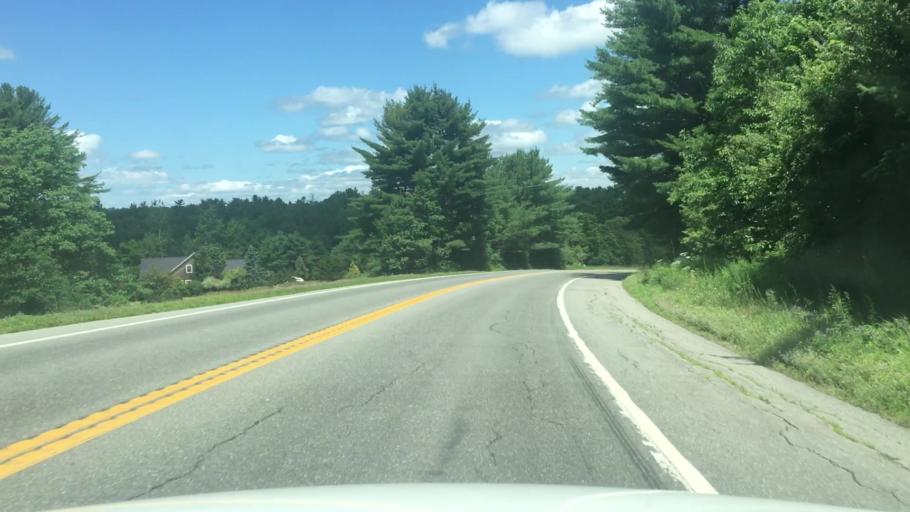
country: US
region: Maine
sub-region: Waldo County
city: Belfast
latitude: 44.3906
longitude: -68.9908
